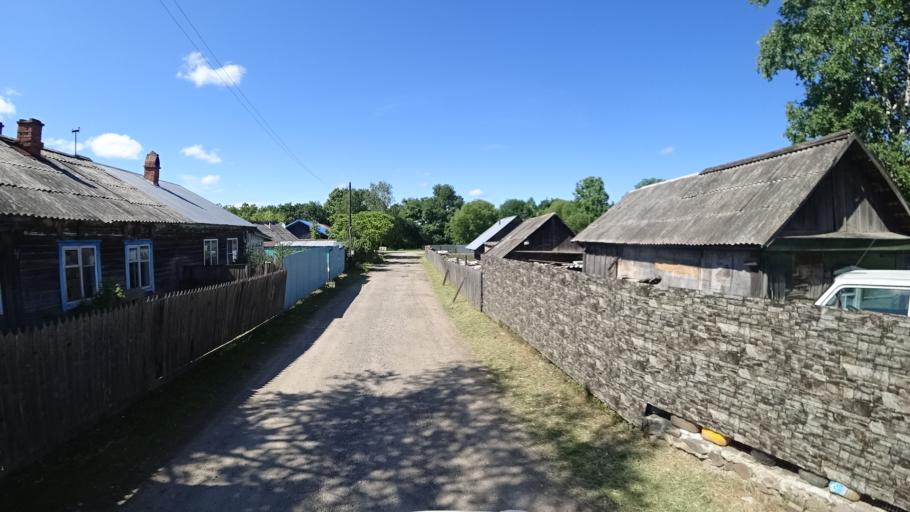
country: RU
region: Khabarovsk Krai
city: Khor
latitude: 47.8884
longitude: 135.0266
